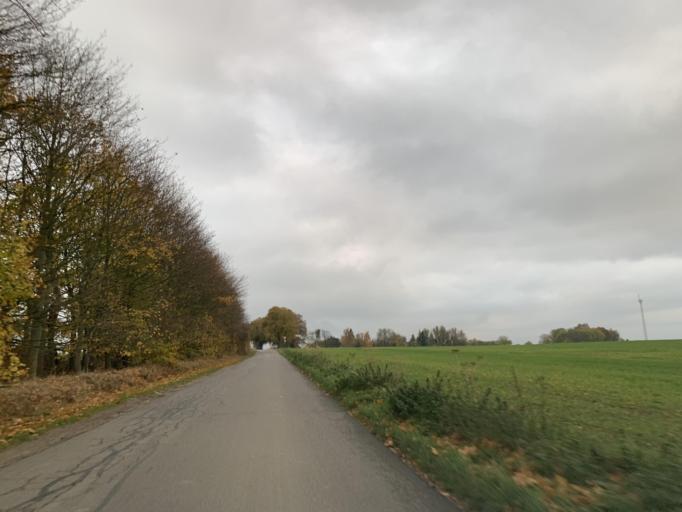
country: DE
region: Mecklenburg-Vorpommern
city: Gross Nemerow
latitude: 53.4699
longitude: 13.2703
